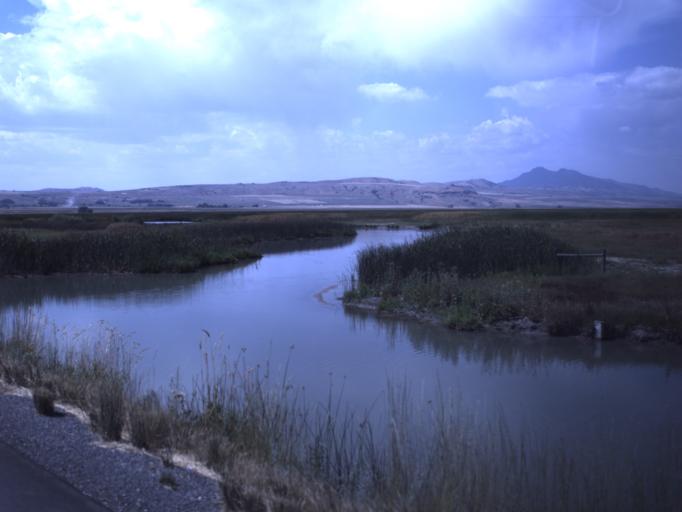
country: US
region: Utah
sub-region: Cache County
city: Benson
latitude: 41.7458
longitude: -111.9337
